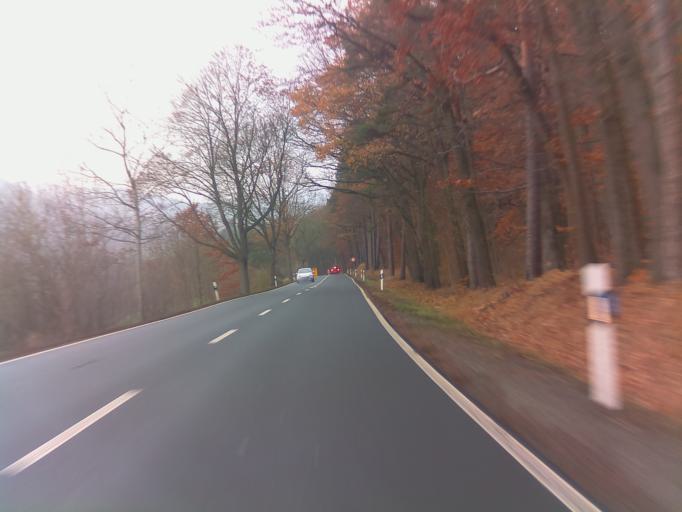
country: DE
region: Thuringia
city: Grimmelshausen
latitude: 50.4875
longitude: 10.6415
